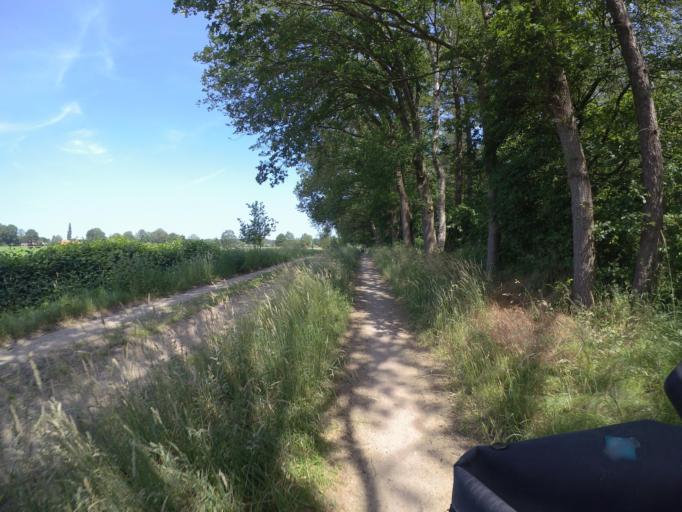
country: NL
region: Overijssel
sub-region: Gemeente Hof van Twente
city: Markelo
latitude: 52.2299
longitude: 6.5235
